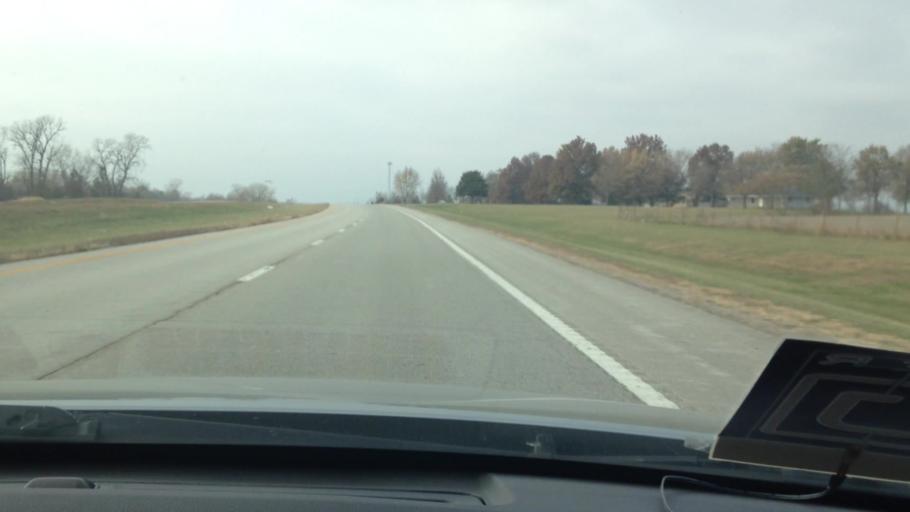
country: US
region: Missouri
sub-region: Cass County
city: Garden City
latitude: 38.5444
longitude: -94.1660
